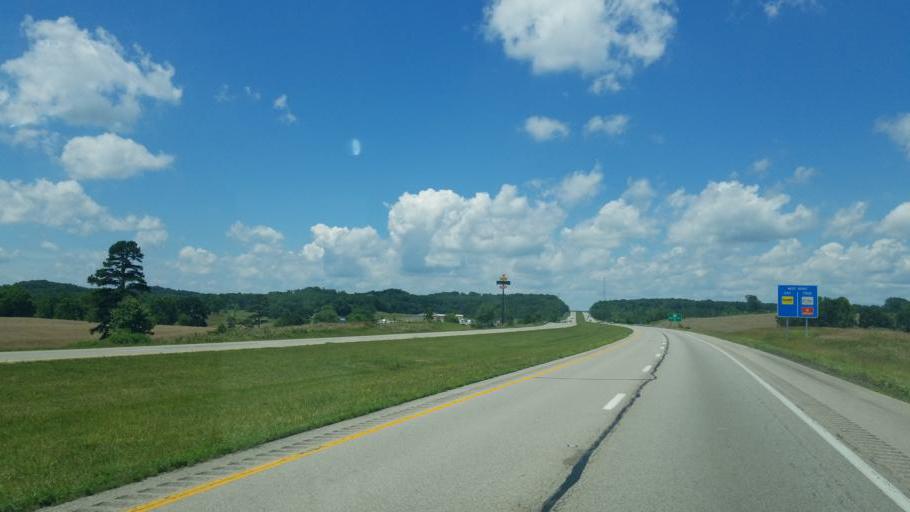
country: US
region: Ohio
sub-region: Gallia County
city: Gallipolis
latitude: 38.8754
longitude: -82.2886
